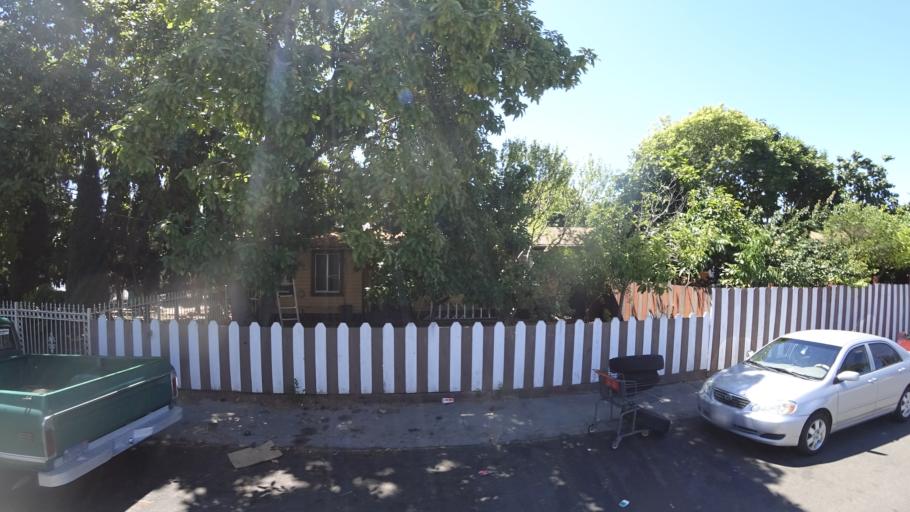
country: US
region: California
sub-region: Alameda County
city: Hayward
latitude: 37.6667
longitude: -122.0900
